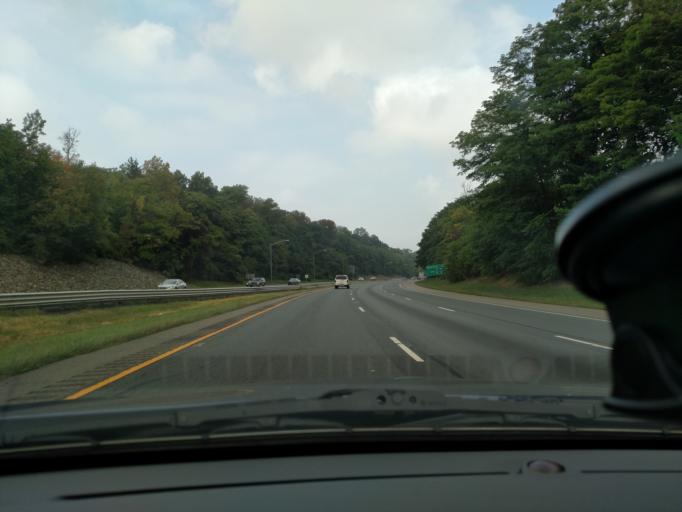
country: US
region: New Jersey
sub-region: Morris County
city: Morristown
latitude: 40.7978
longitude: -74.4386
